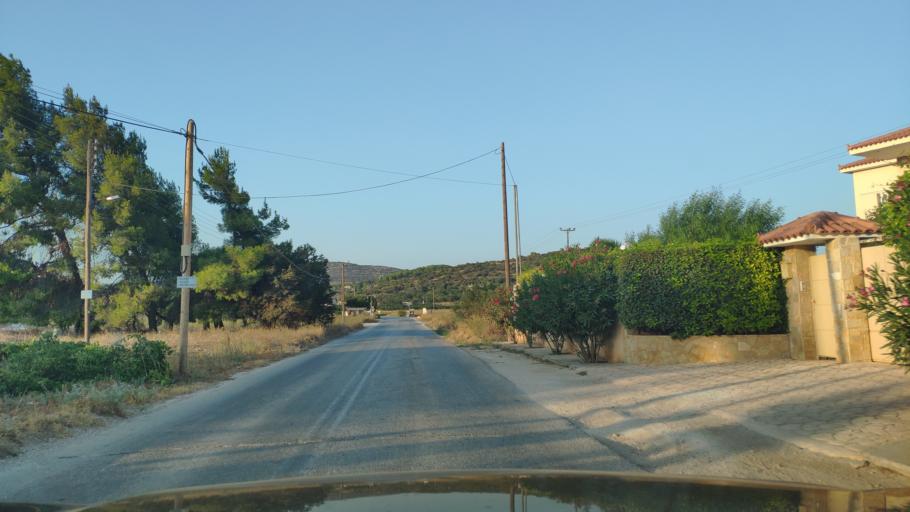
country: GR
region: Attica
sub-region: Nomarchia Anatolikis Attikis
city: Limin Mesoyaias
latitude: 37.9241
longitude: 23.9780
